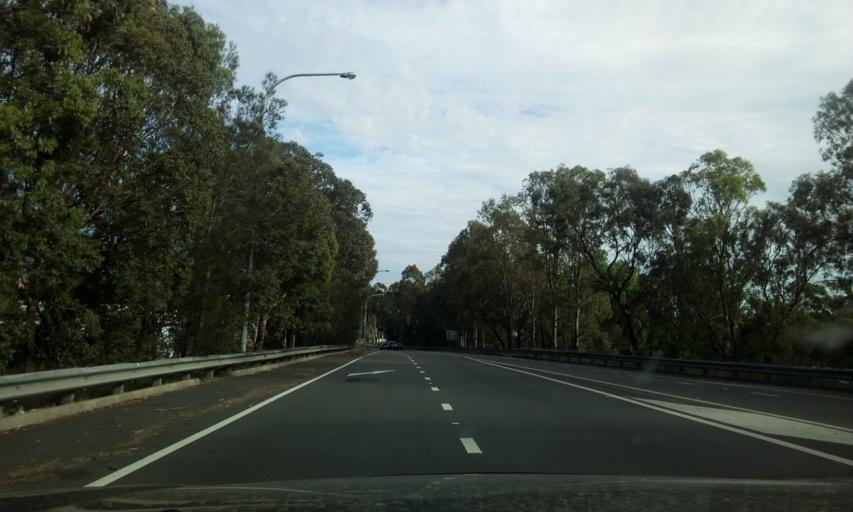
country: AU
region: New South Wales
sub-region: Bankstown
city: Milperra
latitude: -33.9409
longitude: 150.9416
